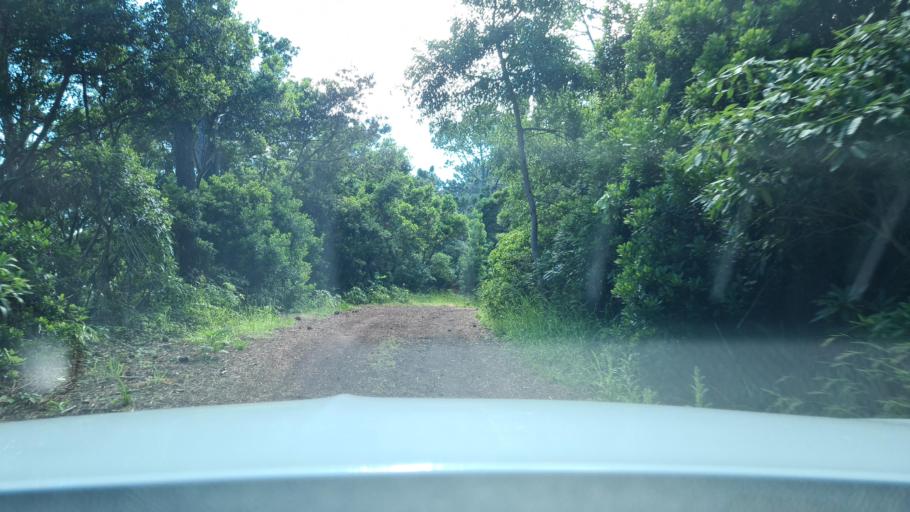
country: PT
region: Azores
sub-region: Sao Roque do Pico
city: Sao Roque do Pico
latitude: 38.4118
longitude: -28.2999
